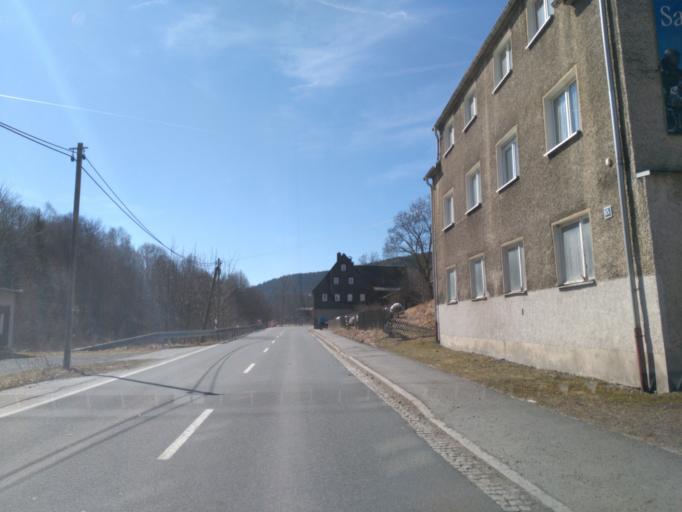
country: CZ
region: Ustecky
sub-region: Okres Chomutov
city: Vejprty
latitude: 50.4703
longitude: 13.0191
